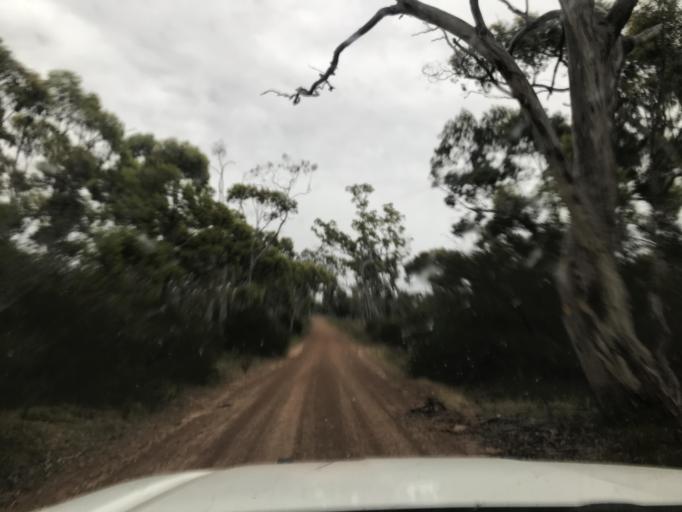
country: AU
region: South Australia
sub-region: Wattle Range
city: Penola
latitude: -37.0936
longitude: 141.5076
